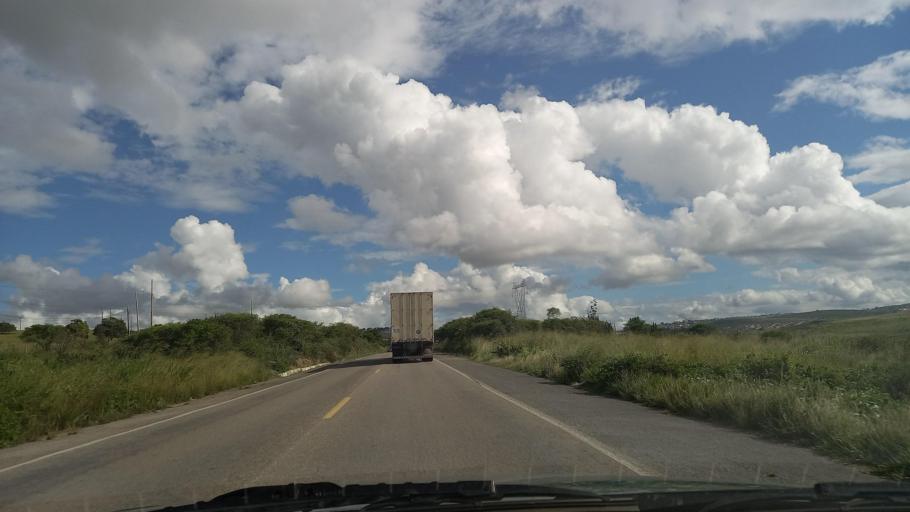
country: BR
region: Pernambuco
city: Garanhuns
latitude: -8.8463
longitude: -36.4604
